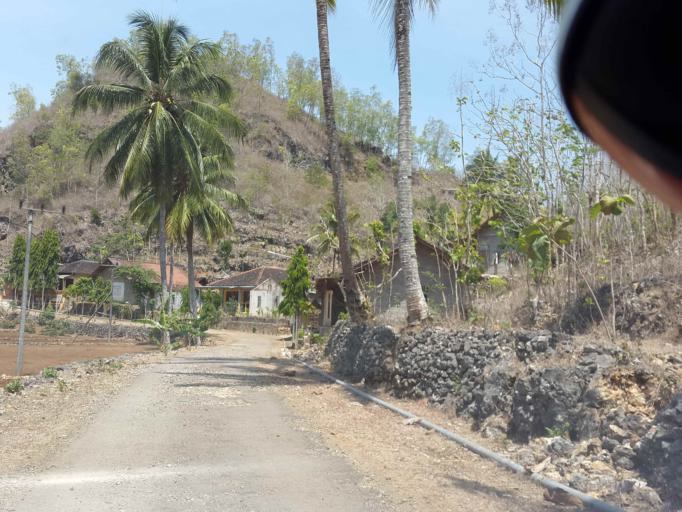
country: ID
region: East Java
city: Krajan
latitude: -8.1730
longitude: 110.9104
